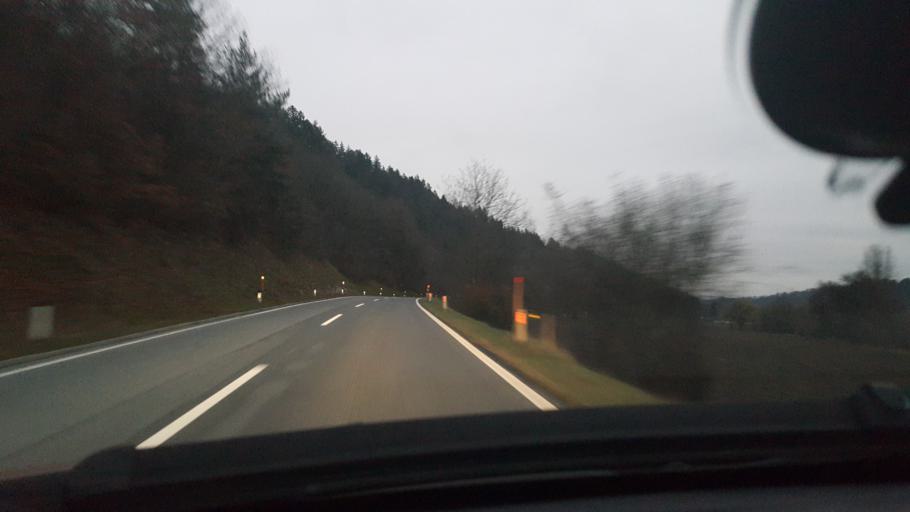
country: AT
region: Carinthia
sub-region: Politischer Bezirk Wolfsberg
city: Lavamund
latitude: 46.6518
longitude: 14.9275
